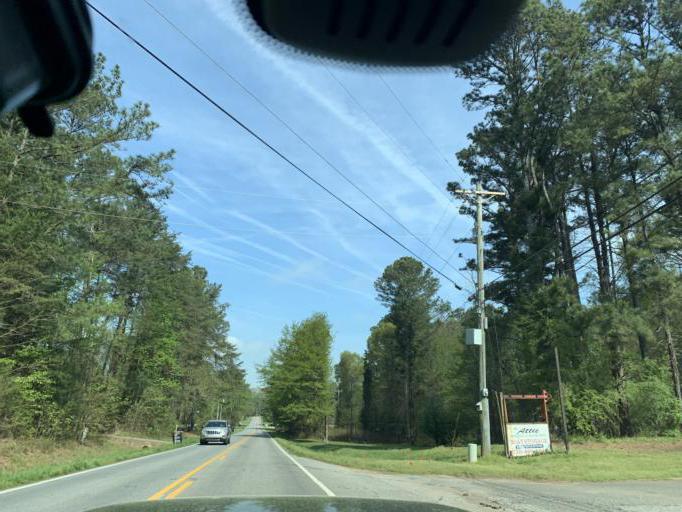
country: US
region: Georgia
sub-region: Forsyth County
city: Cumming
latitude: 34.2139
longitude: -84.0769
